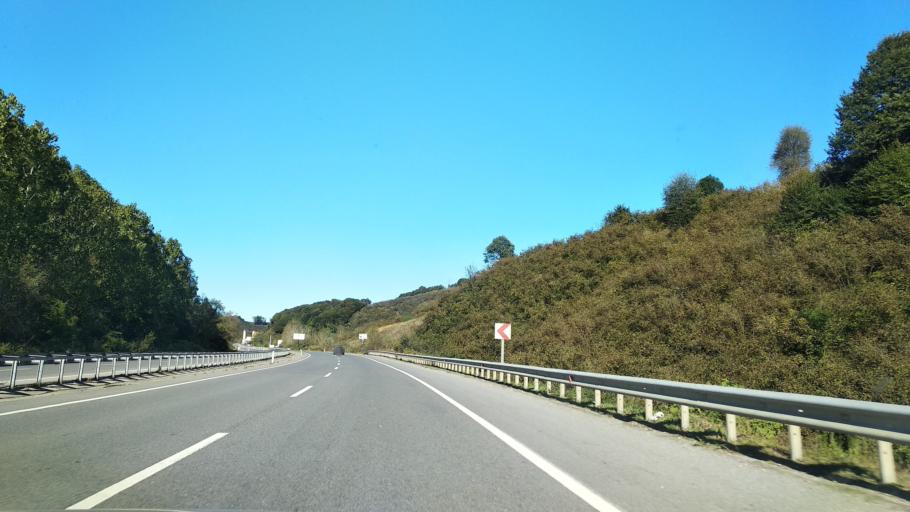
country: TR
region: Sakarya
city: Karasu
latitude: 41.0656
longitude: 30.6425
